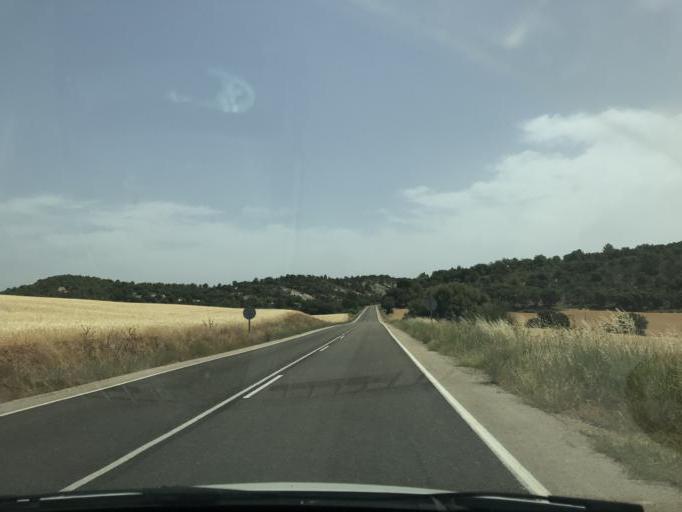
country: ES
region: Castille-La Mancha
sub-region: Provincia de Cuenca
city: La Frontera
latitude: 40.3995
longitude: -2.2521
